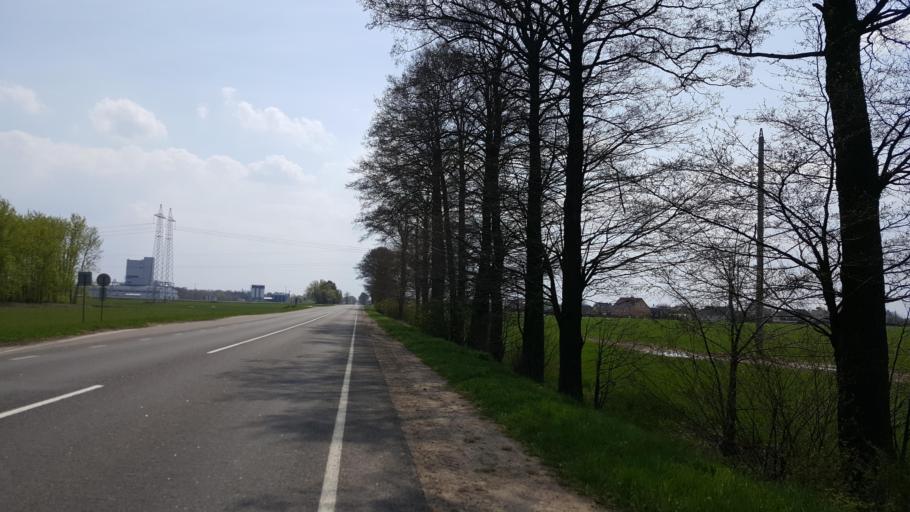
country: BY
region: Brest
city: Zhabinka
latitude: 52.2142
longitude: 23.9977
